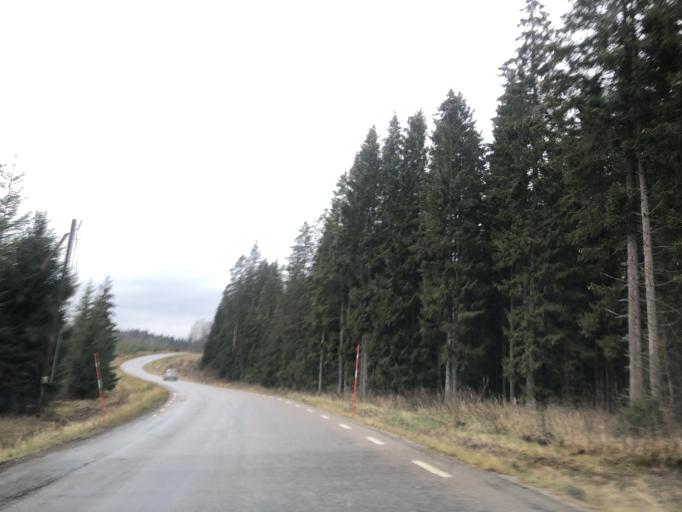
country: SE
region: Vaestra Goetaland
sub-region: Ulricehamns Kommun
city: Ulricehamn
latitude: 57.8973
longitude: 13.4979
